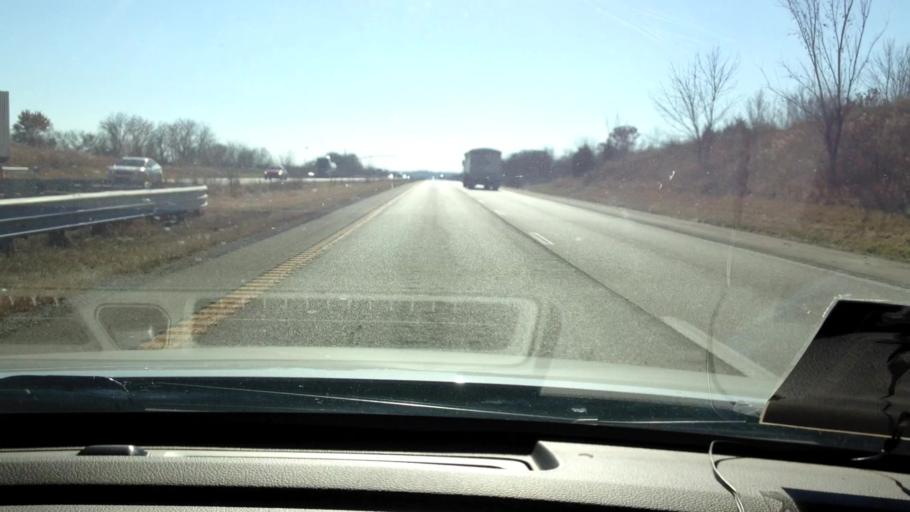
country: US
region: Missouri
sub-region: Platte County
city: Platte City
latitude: 39.4190
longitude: -94.7898
